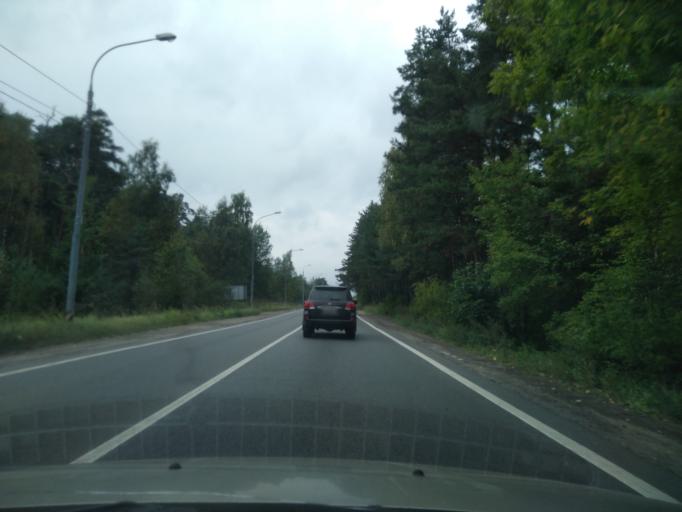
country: RU
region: Moscow
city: Rublevo
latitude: 55.7752
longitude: 37.3584
